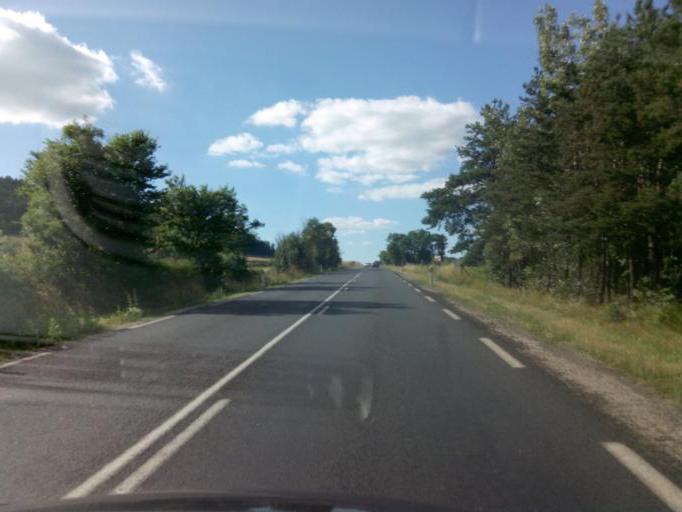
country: FR
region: Auvergne
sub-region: Departement de la Haute-Loire
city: Polignac
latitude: 45.0859
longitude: 3.8172
